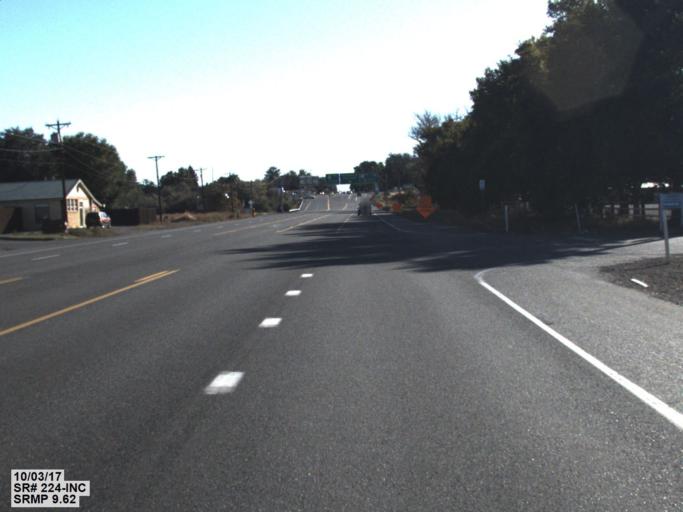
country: US
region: Washington
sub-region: Benton County
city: Richland
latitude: 46.2931
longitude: -119.3110
